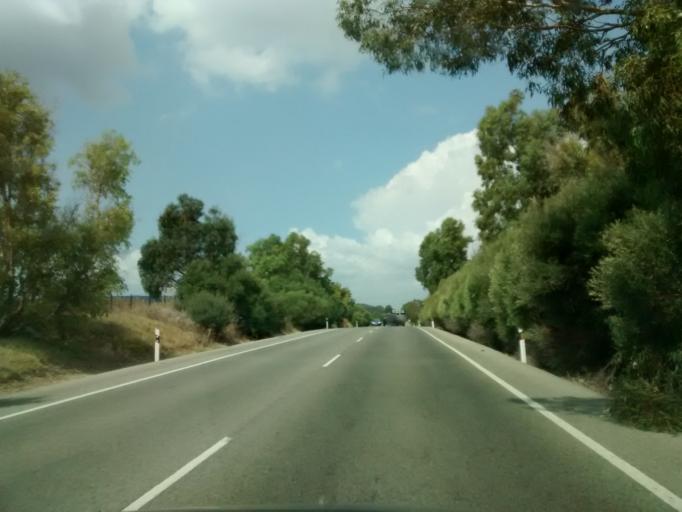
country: ES
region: Andalusia
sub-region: Provincia de Cadiz
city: Zahara de los Atunes
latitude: 36.2007
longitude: -5.7772
